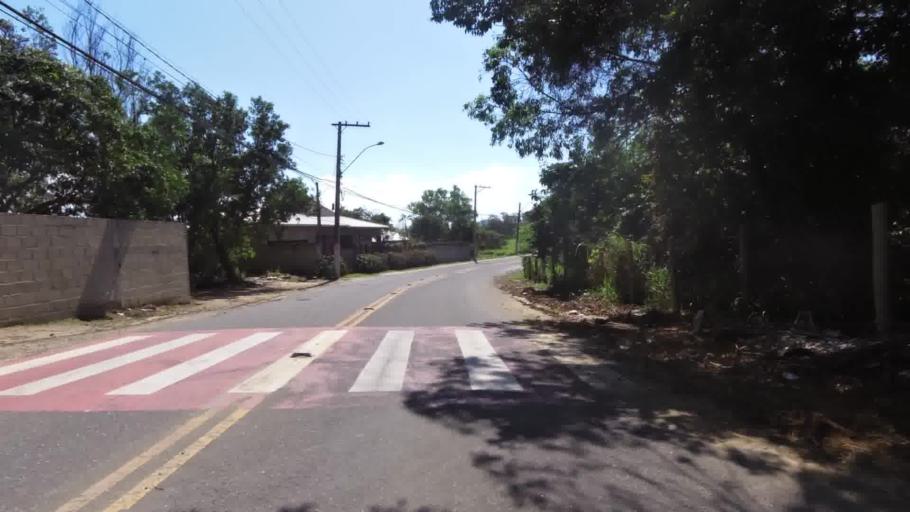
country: BR
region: Espirito Santo
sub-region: Piuma
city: Piuma
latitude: -20.8225
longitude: -40.6286
